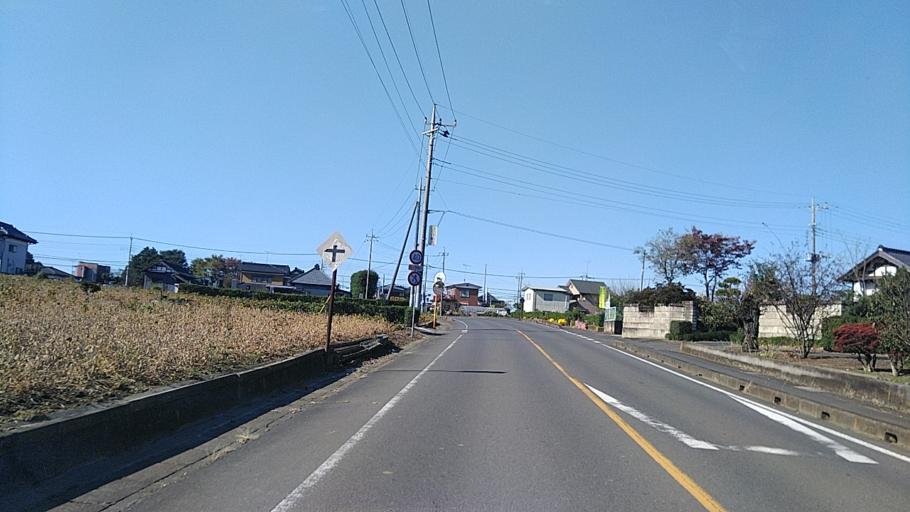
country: JP
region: Ibaraki
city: Shimodate
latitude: 36.2713
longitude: 139.9729
